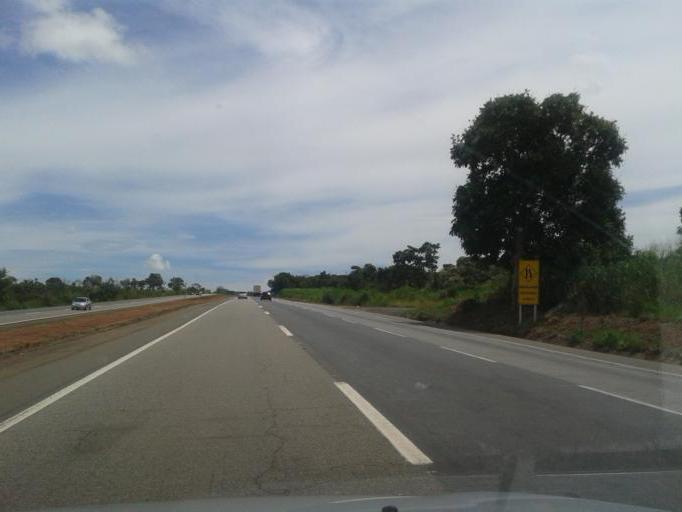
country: BR
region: Goias
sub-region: Hidrolandia
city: Hidrolandia
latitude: -17.0671
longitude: -49.2246
